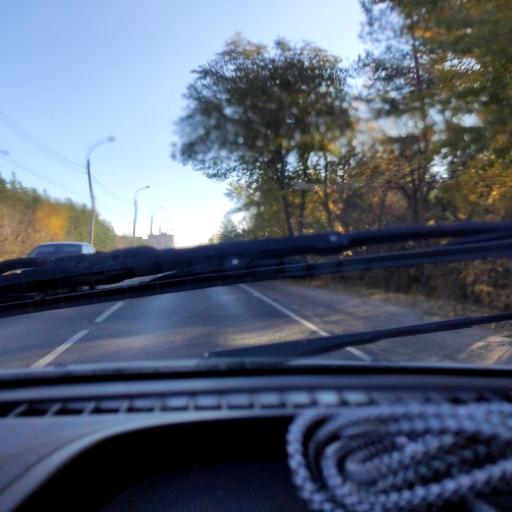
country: RU
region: Samara
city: Zhigulevsk
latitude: 53.4780
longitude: 49.4430
